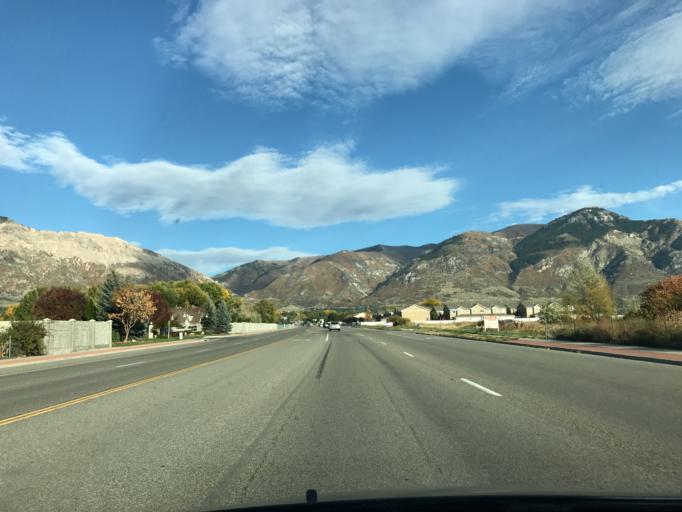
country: US
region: Utah
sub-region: Weber County
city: Pleasant View
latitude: 41.3057
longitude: -111.9866
